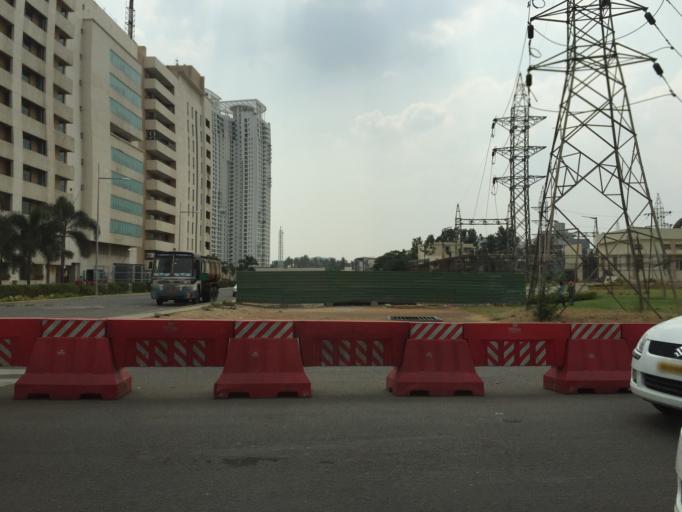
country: IN
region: Karnataka
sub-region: Bangalore Urban
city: Yelahanka
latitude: 13.0477
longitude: 77.6200
